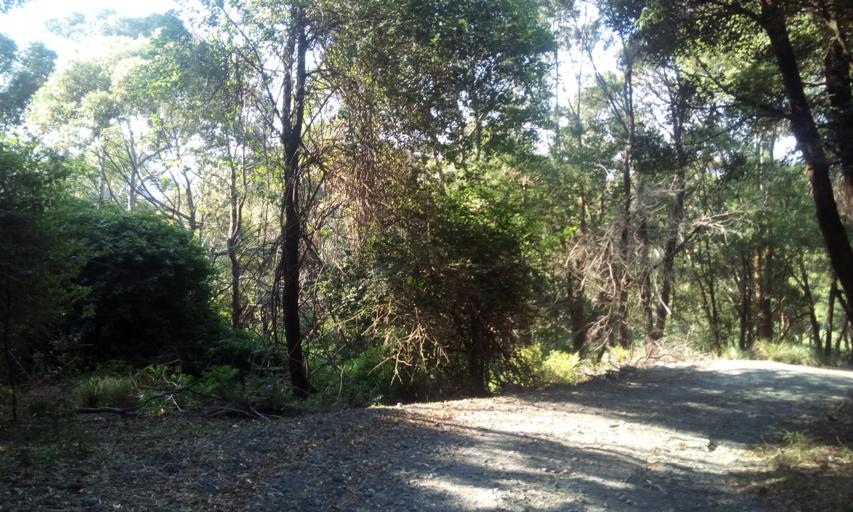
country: AU
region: New South Wales
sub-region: Wollongong
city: Mount Ousley
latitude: -34.3985
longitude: 150.8614
